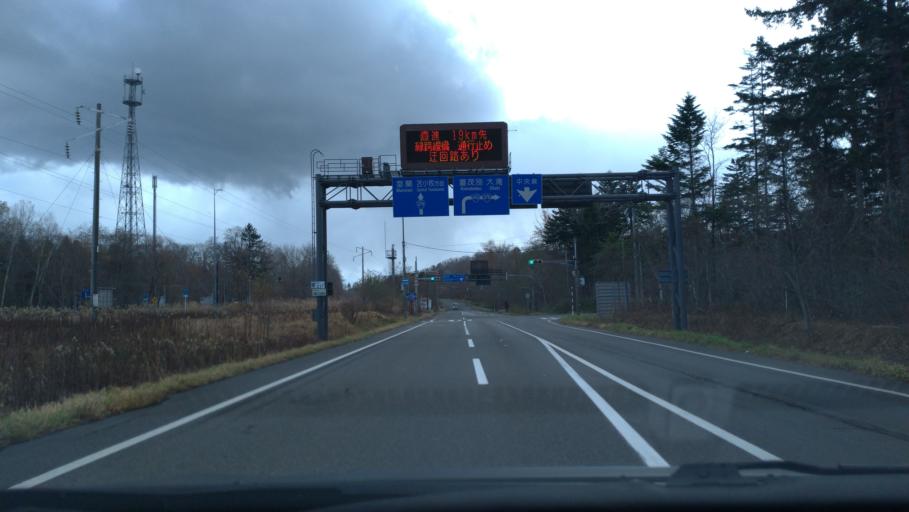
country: JP
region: Hokkaido
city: Tomakomai
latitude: 42.7573
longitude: 141.4394
